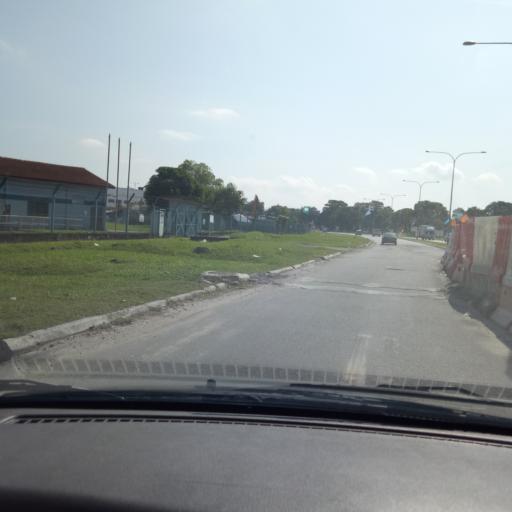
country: MY
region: Selangor
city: Kampong Baharu Balakong
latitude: 3.0174
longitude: 101.7634
